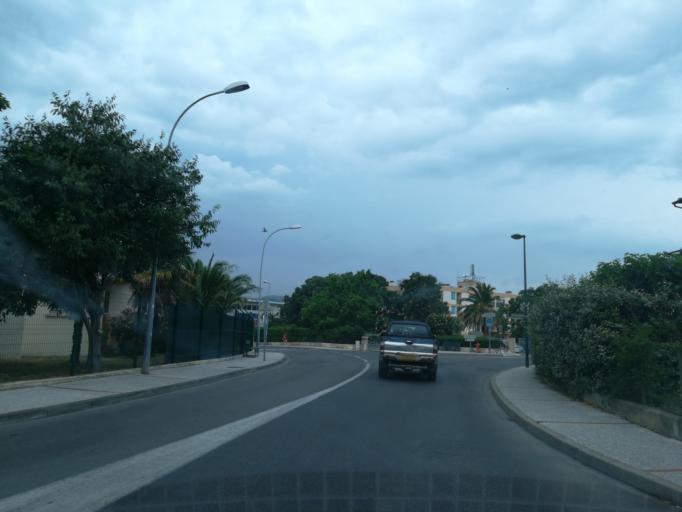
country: FR
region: Languedoc-Roussillon
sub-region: Departement des Pyrenees-Orientales
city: Ceret
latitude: 42.4892
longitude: 2.7527
